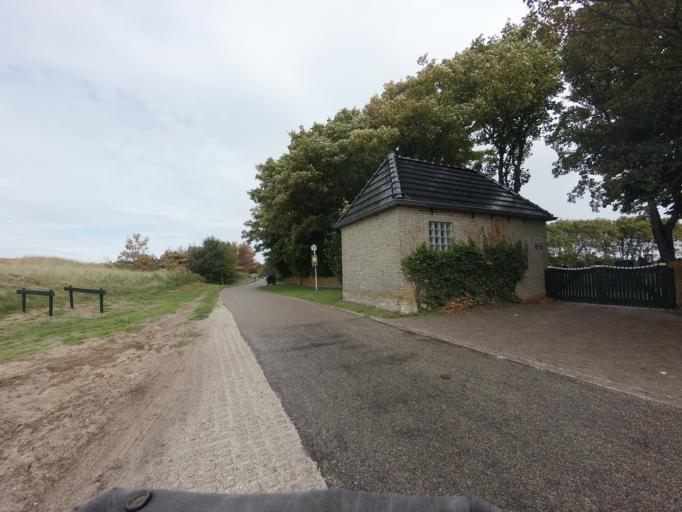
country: NL
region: Friesland
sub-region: Gemeente Ameland
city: Nes
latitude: 53.4482
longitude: 5.7816
